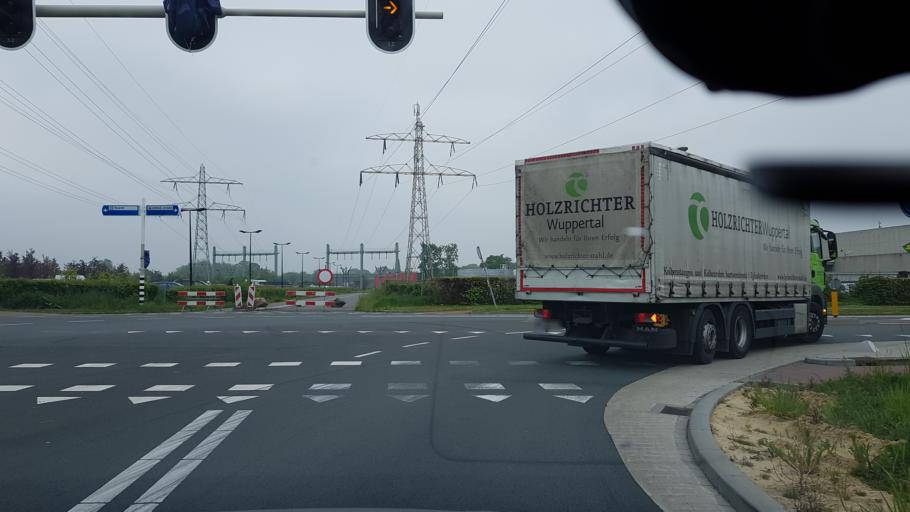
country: NL
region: Limburg
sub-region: Gemeente Meerssen
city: Meerssen
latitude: 50.8737
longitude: 5.7181
